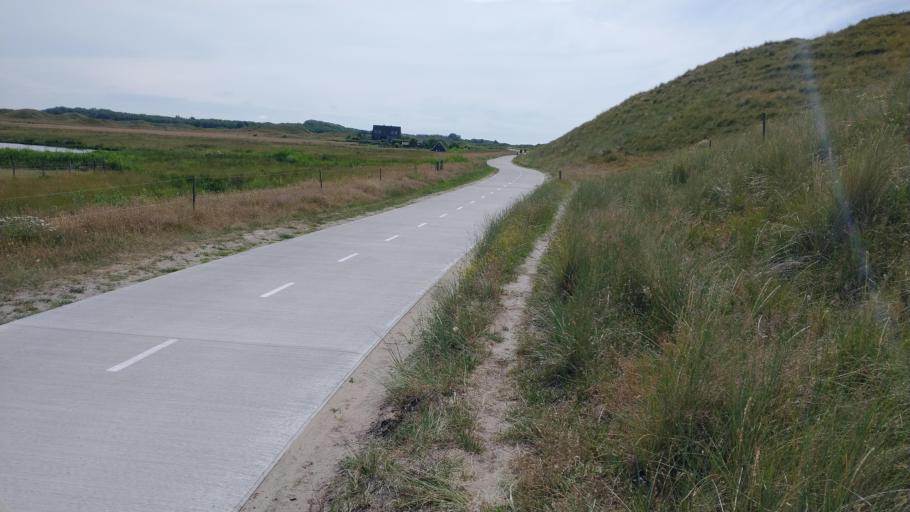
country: NL
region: North Holland
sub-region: Gemeente Texel
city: Den Burg
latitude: 53.1144
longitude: 4.7973
